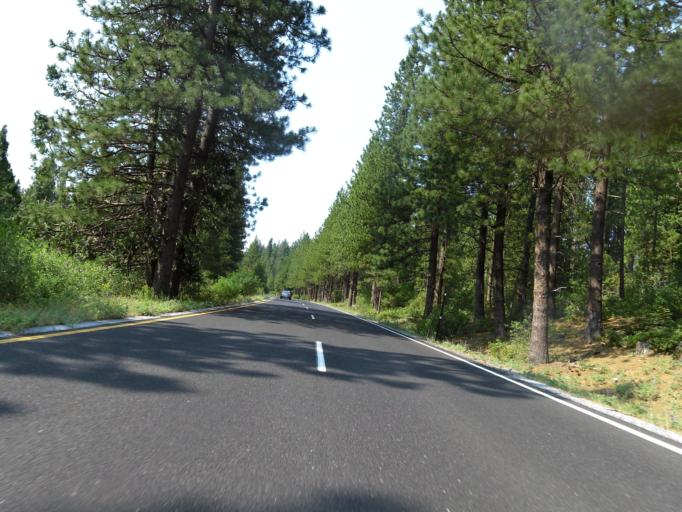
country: US
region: California
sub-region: Tuolumne County
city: Twain Harte
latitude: 38.1147
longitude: -120.1215
